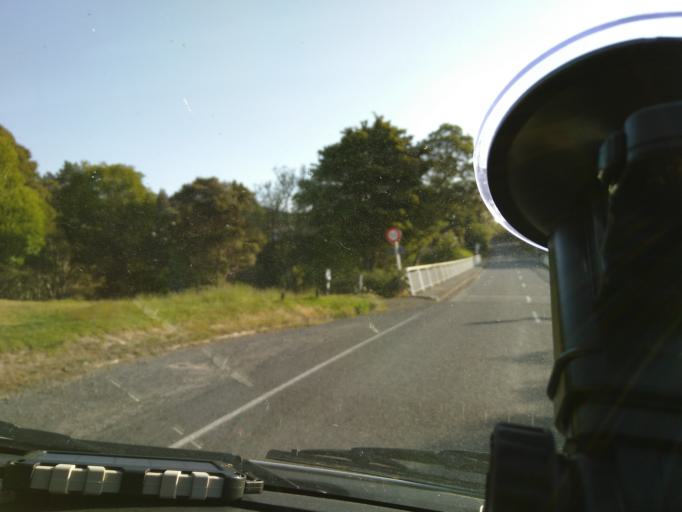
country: NZ
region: Northland
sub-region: Far North District
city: Paihia
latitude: -35.2776
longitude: 174.0512
